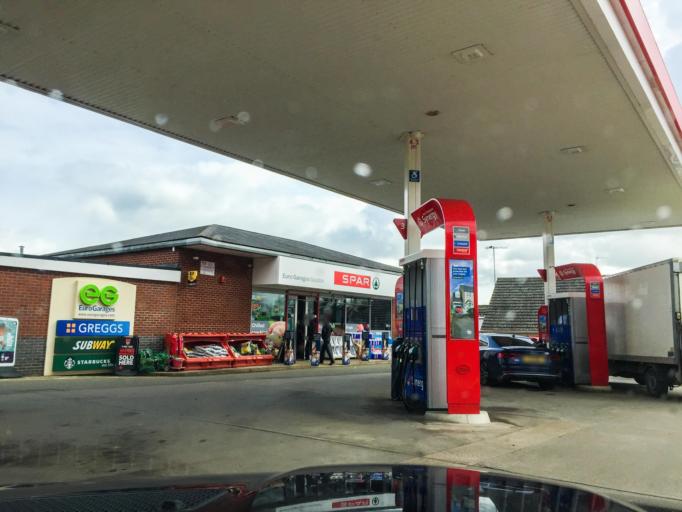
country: GB
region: England
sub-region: Warwickshire
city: Harbury
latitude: 52.1840
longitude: -1.4658
